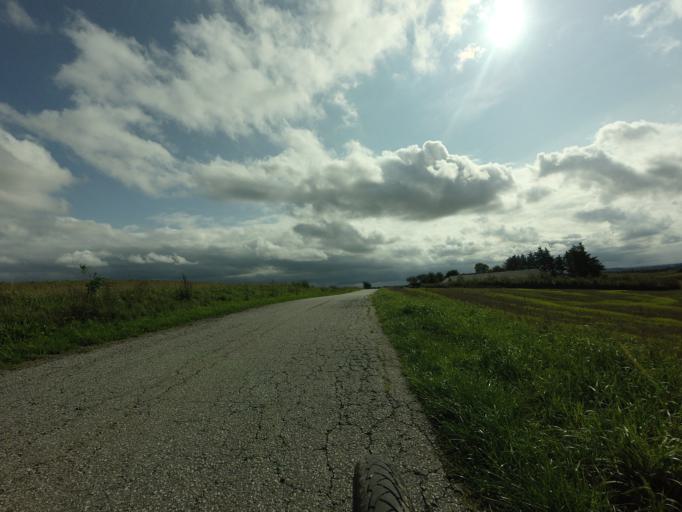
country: DK
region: North Denmark
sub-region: Hjorring Kommune
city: Hjorring
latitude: 57.5314
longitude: 10.0401
